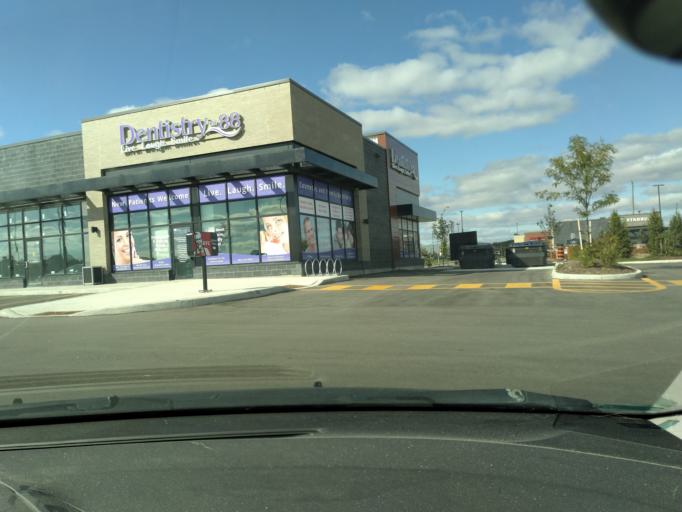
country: CA
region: Ontario
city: Bradford West Gwillimbury
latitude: 44.1067
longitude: -79.5923
